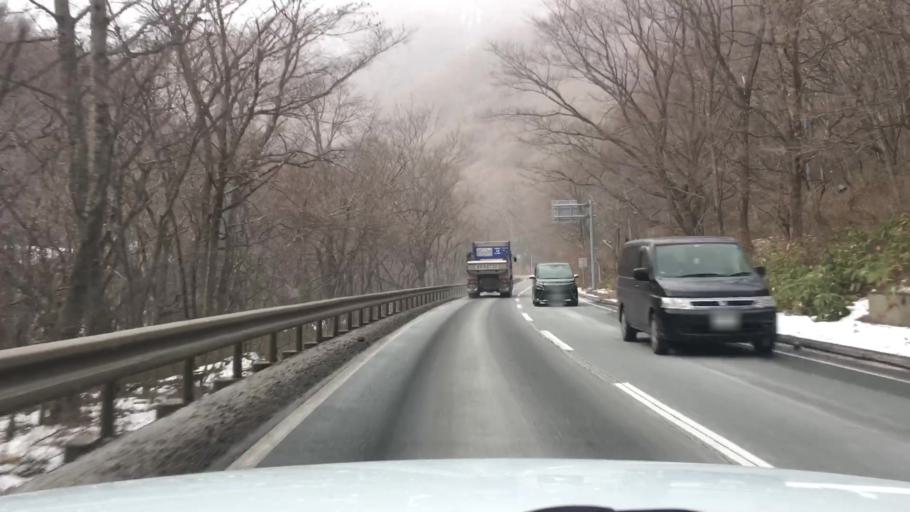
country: JP
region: Iwate
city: Tono
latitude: 39.6173
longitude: 141.4980
